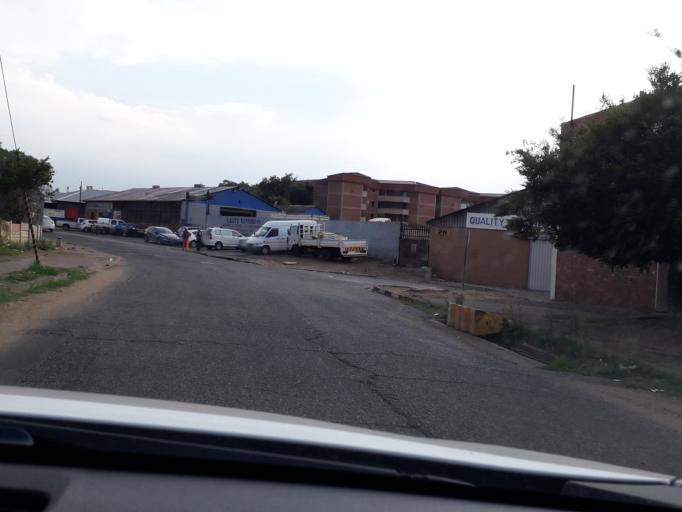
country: ZA
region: Gauteng
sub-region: City of Johannesburg Metropolitan Municipality
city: Johannesburg
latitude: -26.1787
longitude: 27.9662
